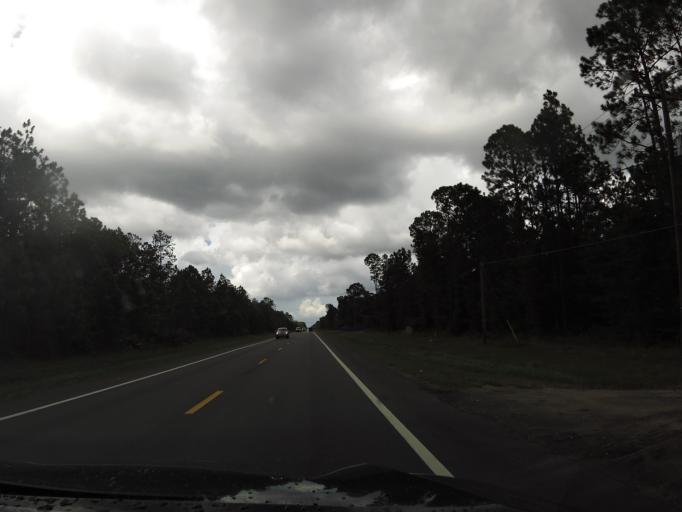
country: US
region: Florida
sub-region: Clay County
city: Asbury Lake
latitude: 30.0356
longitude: -81.8284
